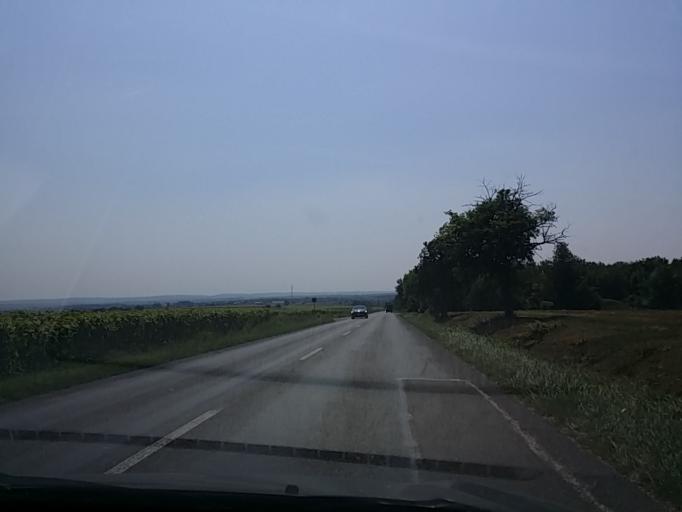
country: HU
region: Tolna
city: Iregszemcse
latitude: 46.7232
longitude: 18.1710
